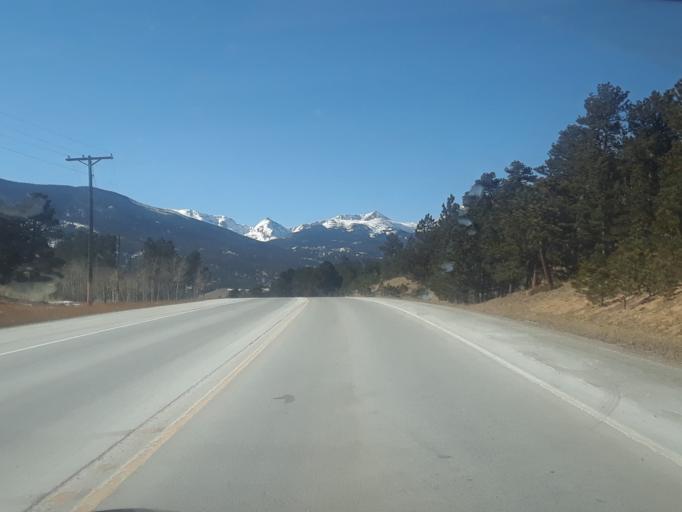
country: US
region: Colorado
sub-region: Larimer County
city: Estes Park
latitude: 40.1885
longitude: -105.4914
